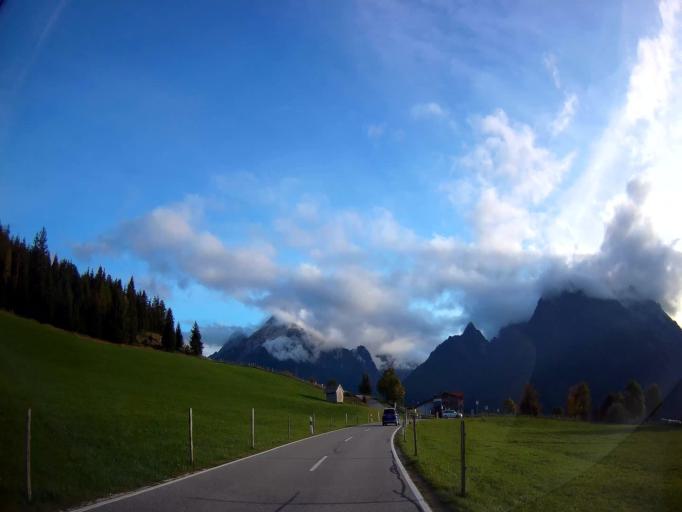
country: DE
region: Bavaria
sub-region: Upper Bavaria
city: Ramsau
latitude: 47.6232
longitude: 12.9040
